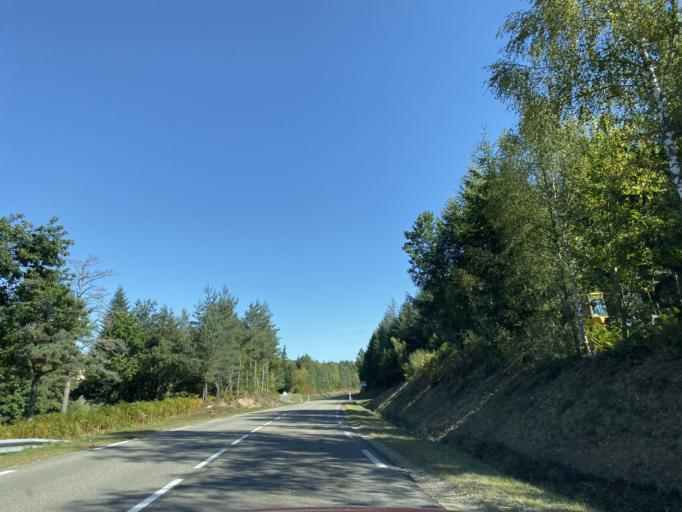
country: FR
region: Rhone-Alpes
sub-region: Departement de la Loire
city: Noiretable
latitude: 45.8388
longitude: 3.7867
